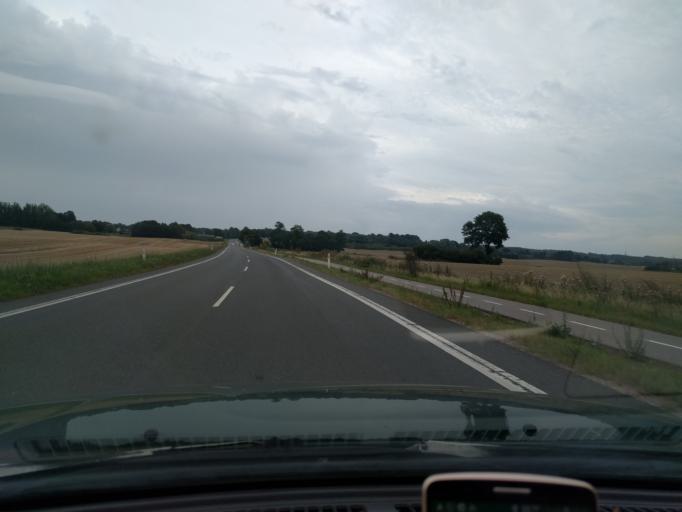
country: DK
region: Zealand
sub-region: Naestved Kommune
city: Fuglebjerg
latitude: 55.2336
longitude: 11.4571
